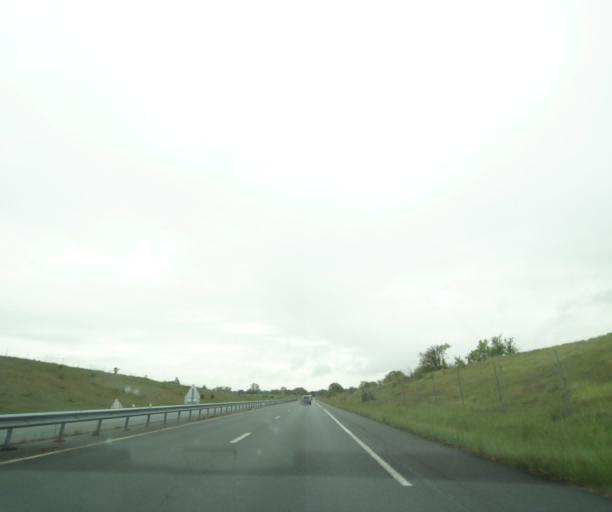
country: FR
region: Poitou-Charentes
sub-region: Departement de la Charente-Maritime
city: Chermignac
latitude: 45.7137
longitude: -0.6884
